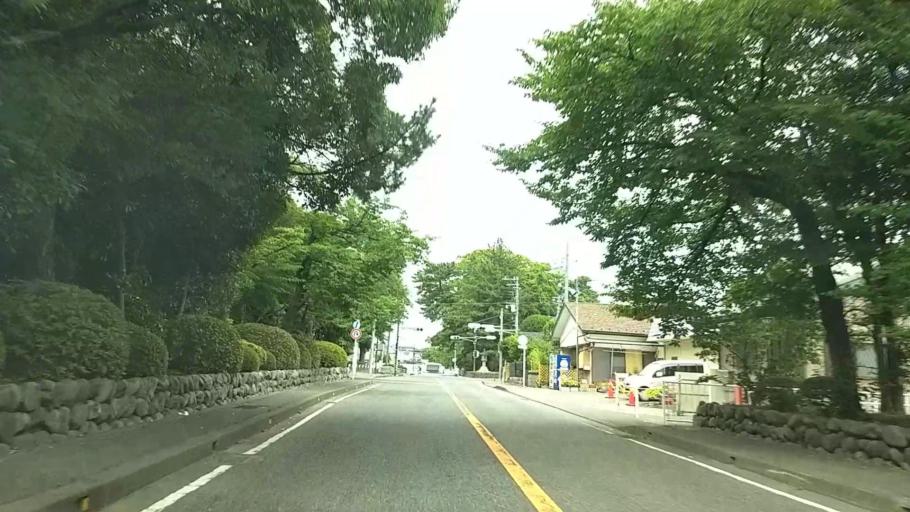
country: JP
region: Kanagawa
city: Chigasaki
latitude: 35.3765
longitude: 139.3810
